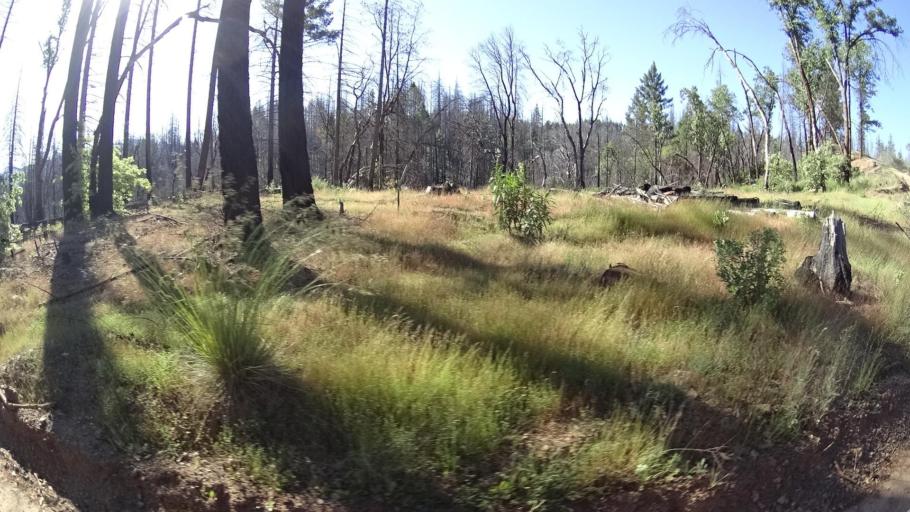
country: US
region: California
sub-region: Lake County
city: Upper Lake
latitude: 39.3907
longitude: -122.9783
